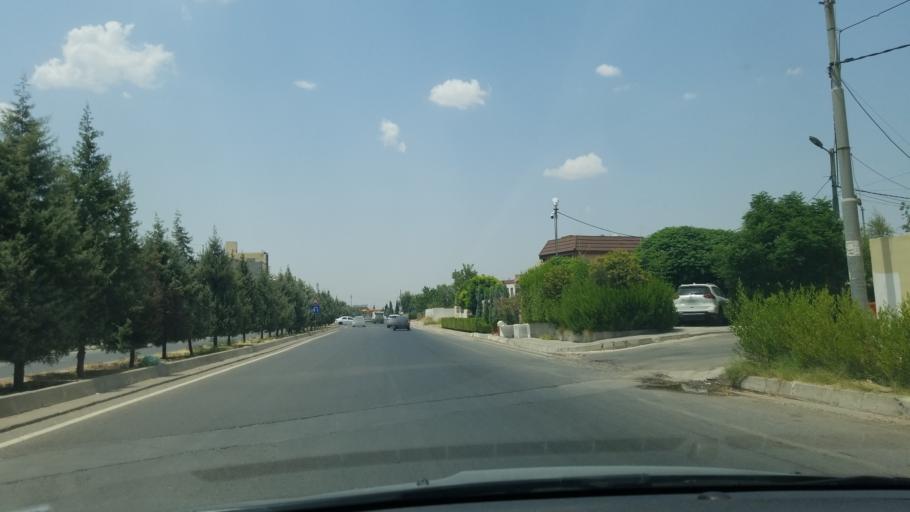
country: IQ
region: Arbil
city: Erbil
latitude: 36.1712
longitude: 44.0586
